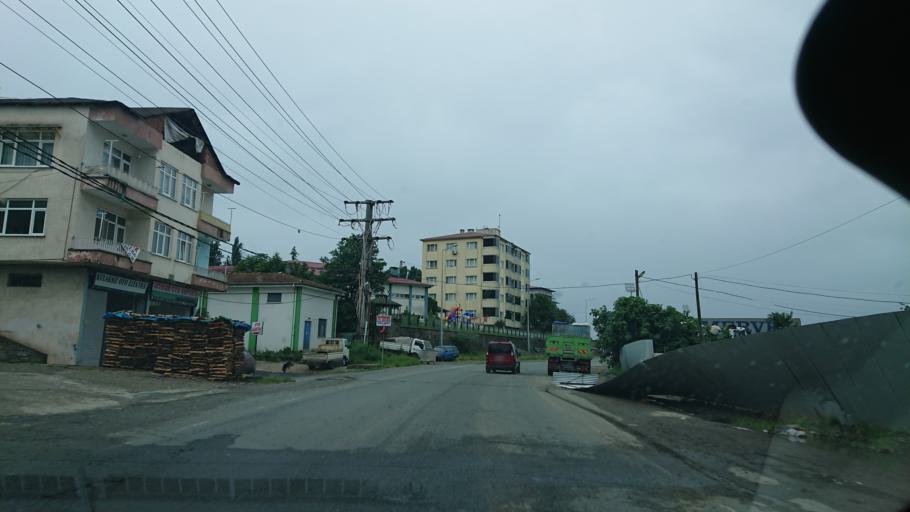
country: TR
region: Rize
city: Gundogdu
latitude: 41.0392
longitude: 40.5766
